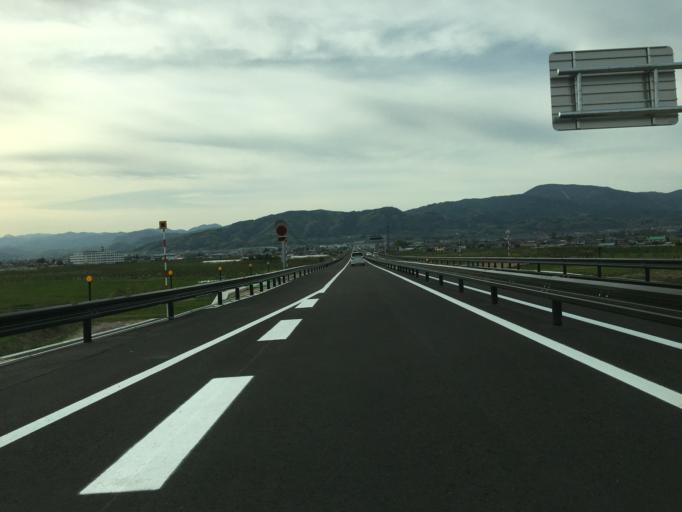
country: JP
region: Fukushima
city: Hobaramachi
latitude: 37.8145
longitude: 140.5328
